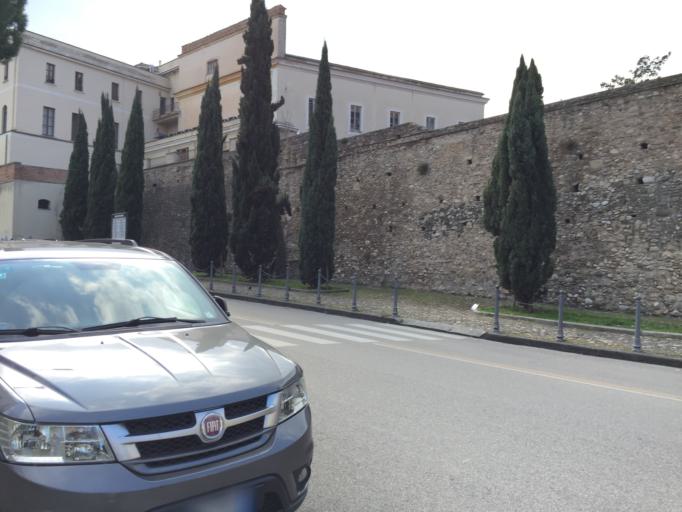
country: IT
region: Campania
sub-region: Provincia di Benevento
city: Benevento
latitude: 41.1318
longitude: 14.7828
